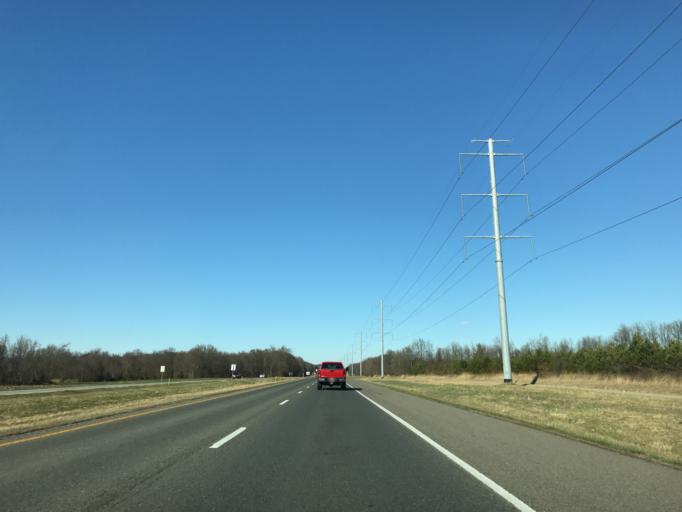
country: US
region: Maryland
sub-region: Queen Anne's County
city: Centreville
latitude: 39.0619
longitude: -75.9936
